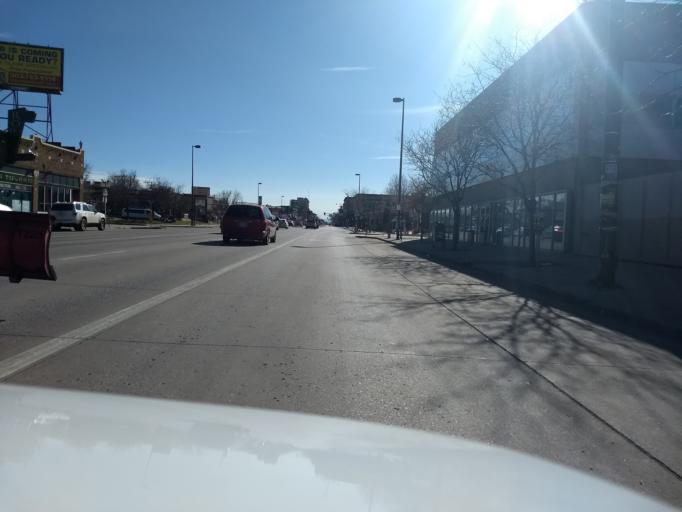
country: US
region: Colorado
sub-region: Denver County
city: Denver
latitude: 39.7231
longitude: -104.9876
